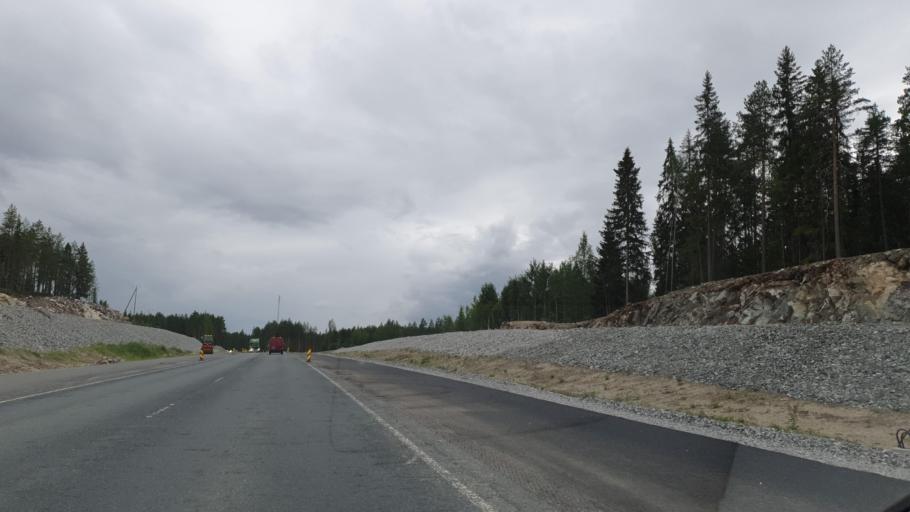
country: FI
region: Northern Savo
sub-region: Ylae-Savo
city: Lapinlahti
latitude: 63.2827
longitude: 27.4555
